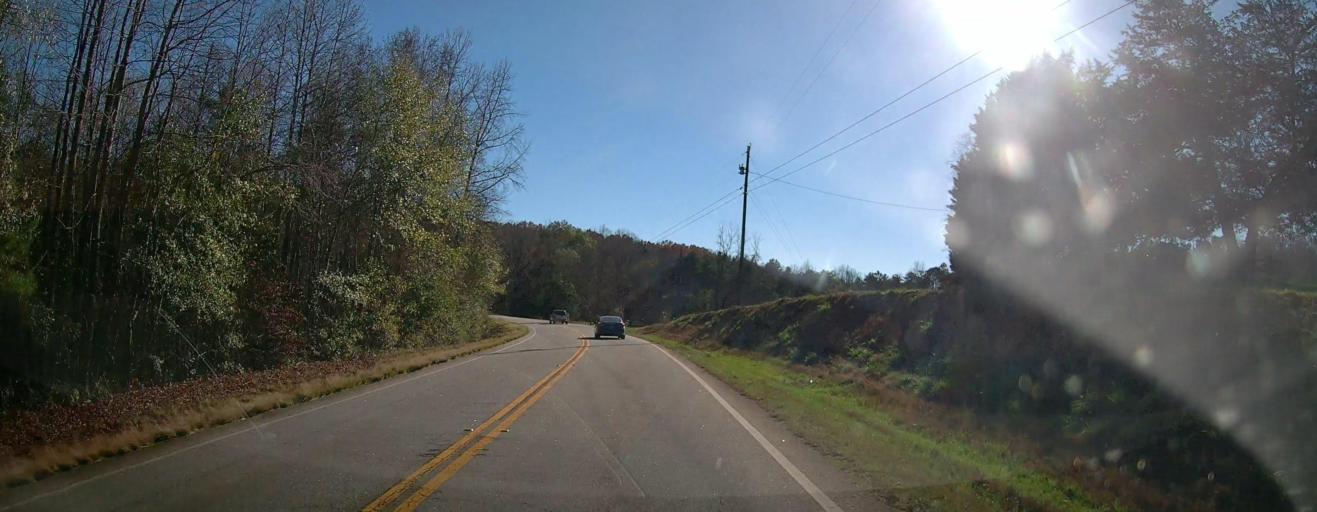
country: US
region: Georgia
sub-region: Hall County
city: Lula
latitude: 34.4106
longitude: -83.7099
